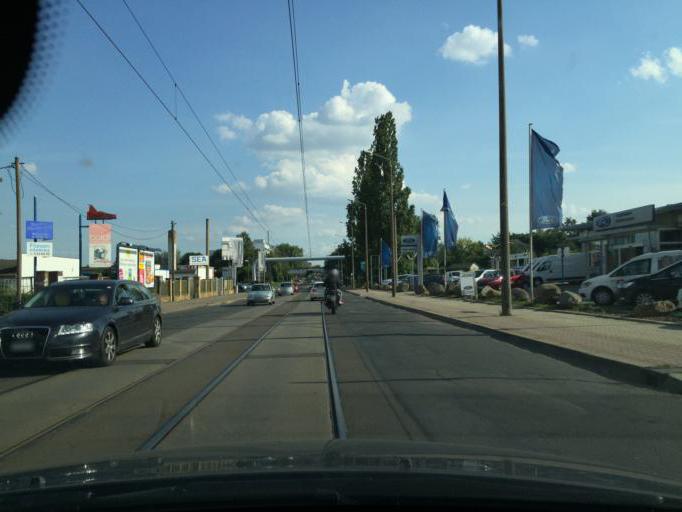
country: DE
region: Saxony
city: Leipzig
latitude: 51.3105
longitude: 12.3260
